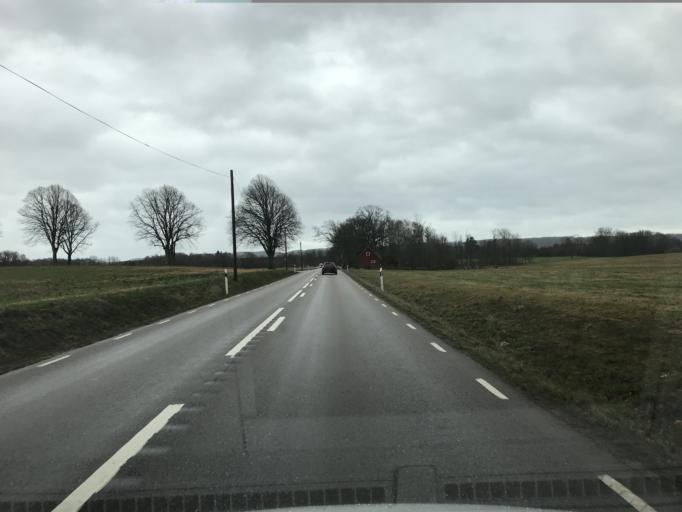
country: SE
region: Skane
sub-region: Klippans Kommun
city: Klippan
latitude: 56.1083
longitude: 13.1777
